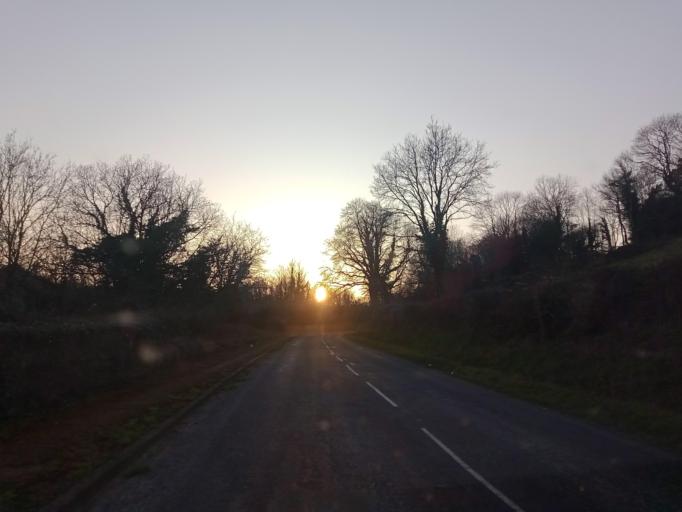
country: IE
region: Leinster
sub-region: Kilkenny
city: Castlecomer
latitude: 52.8080
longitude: -7.2180
